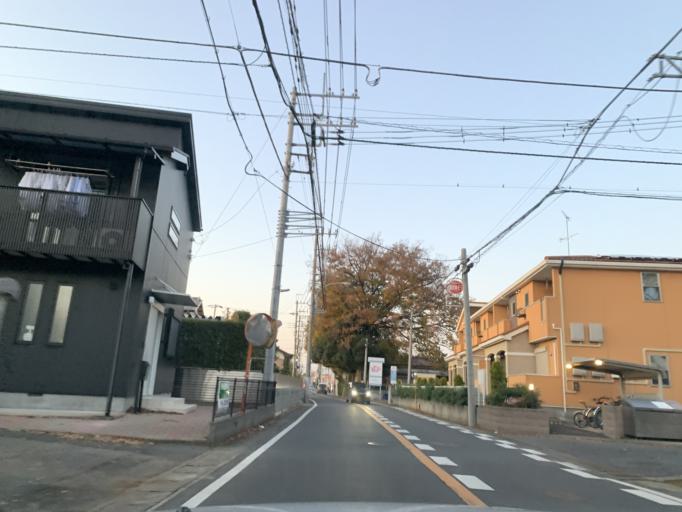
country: JP
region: Chiba
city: Nagareyama
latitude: 35.9052
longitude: 139.9048
